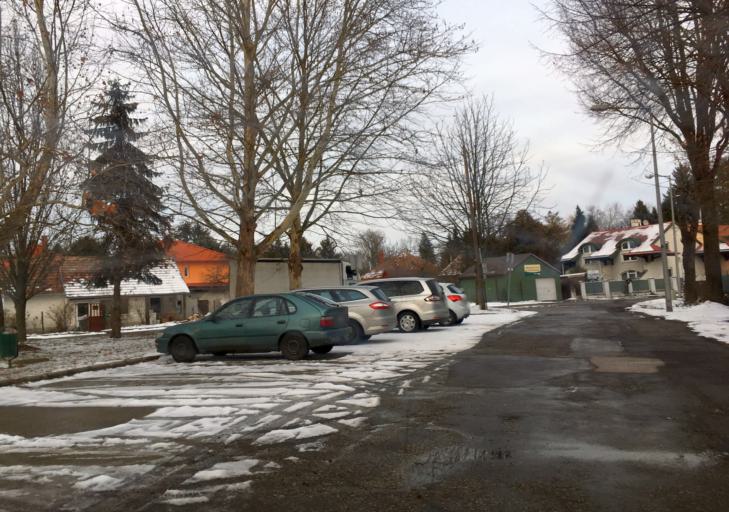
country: HU
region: Gyor-Moson-Sopron
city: Mosonmagyarovar
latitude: 47.8768
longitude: 17.2795
